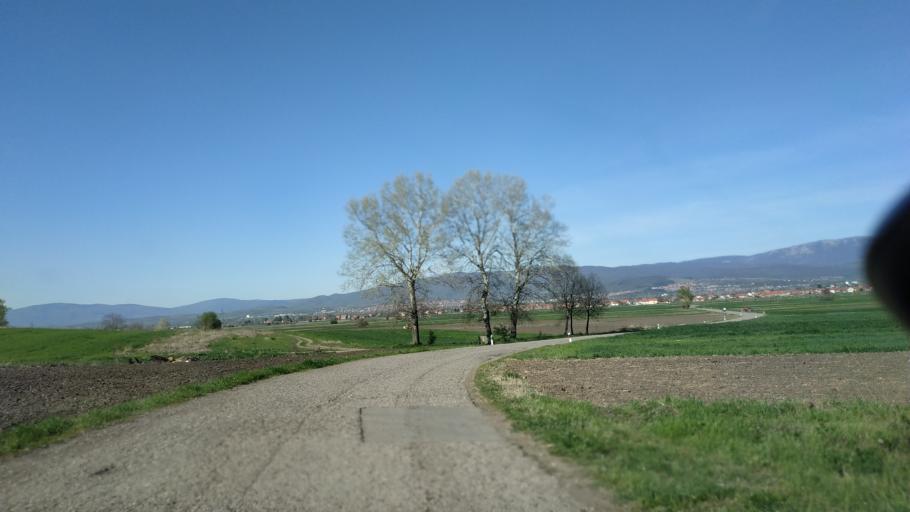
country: RS
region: Central Serbia
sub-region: Nisavski Okrug
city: Aleksinac
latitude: 43.4989
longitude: 21.6748
